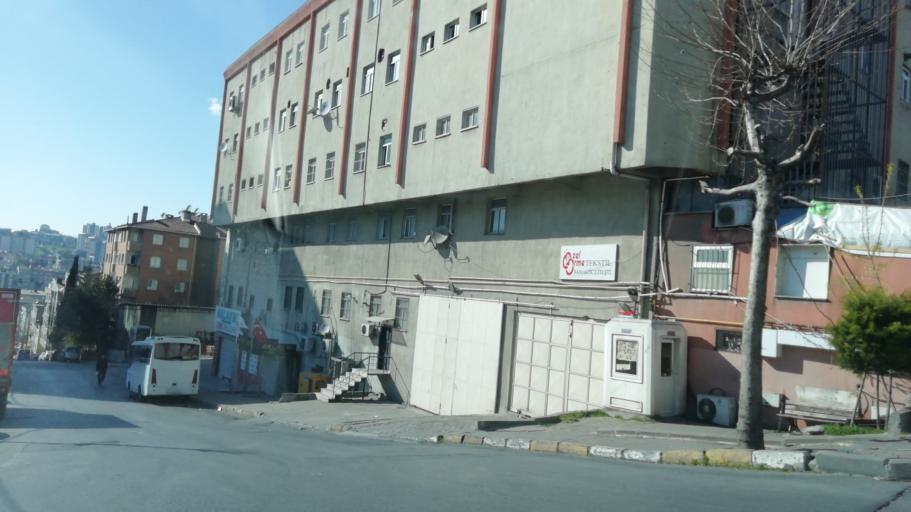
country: TR
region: Istanbul
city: Bagcilar
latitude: 41.0366
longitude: 28.8523
